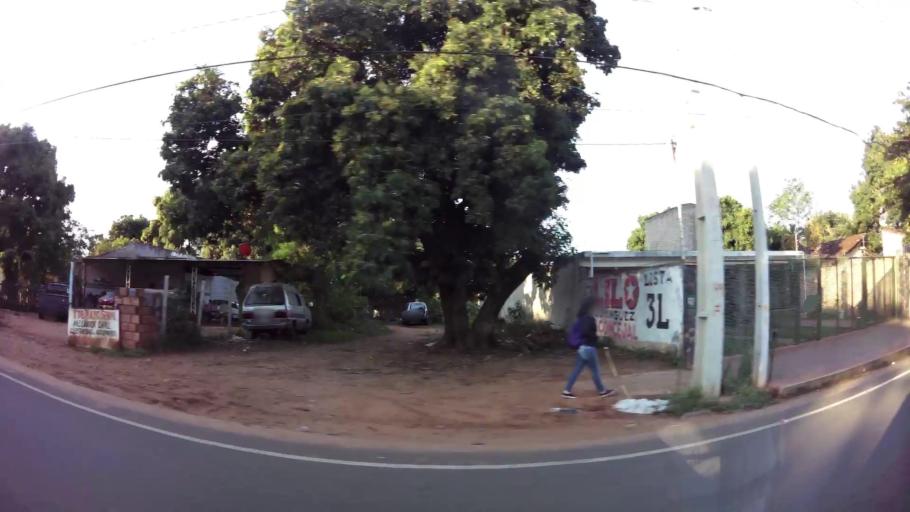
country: PY
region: Central
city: San Lorenzo
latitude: -25.3593
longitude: -57.5105
